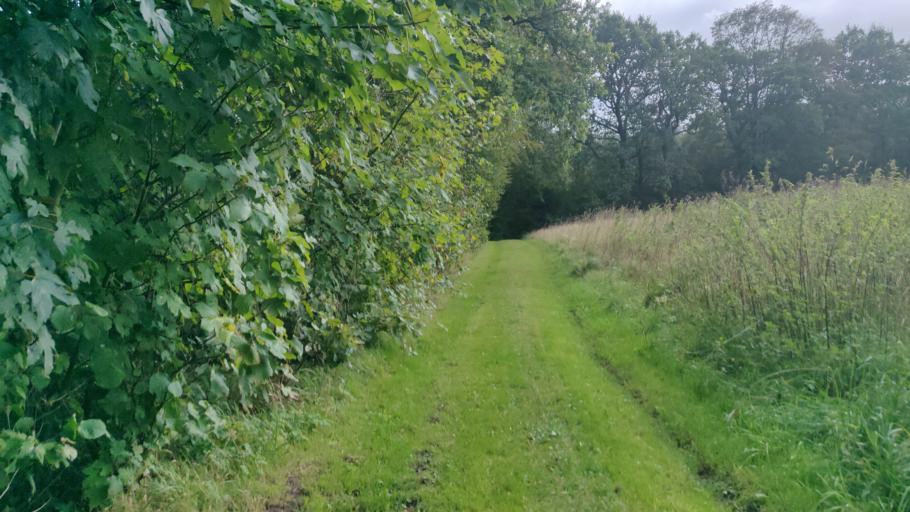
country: DK
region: South Denmark
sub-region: Kolding Kommune
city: Lunderskov
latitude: 55.5473
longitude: 9.3579
